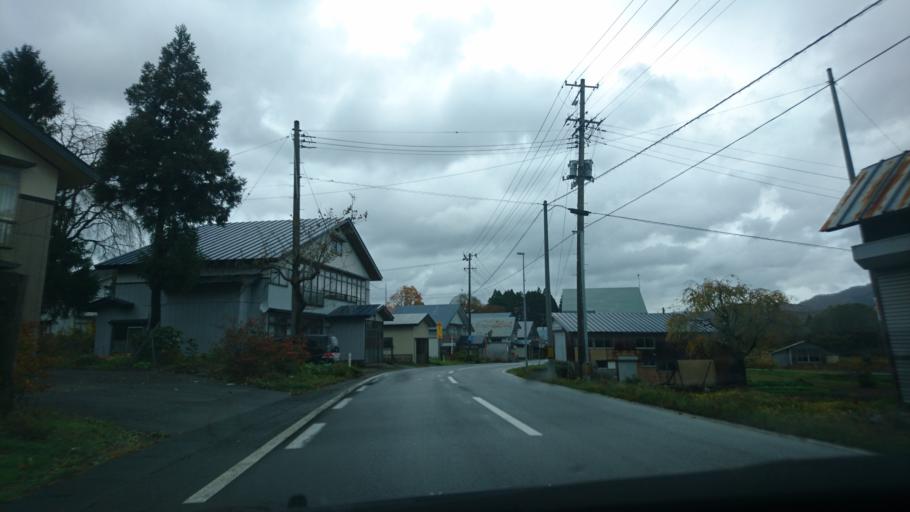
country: JP
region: Akita
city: Kakunodatemachi
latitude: 39.4587
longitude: 140.7726
